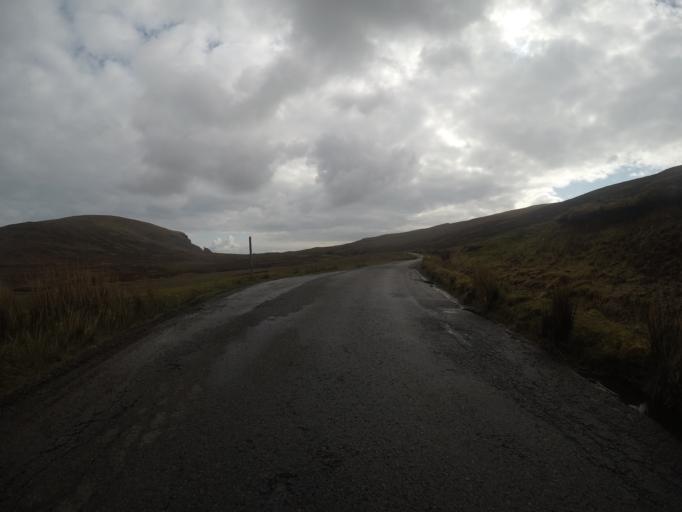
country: GB
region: Scotland
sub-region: Highland
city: Portree
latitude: 57.6229
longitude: -6.3096
